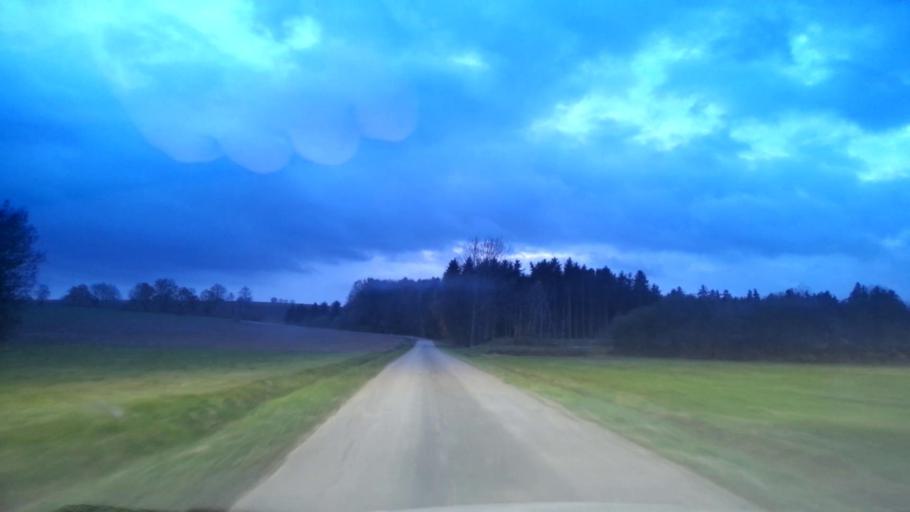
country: DE
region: Bavaria
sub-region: Upper Palatinate
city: Fuchsmuhl
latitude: 49.9265
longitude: 12.1637
